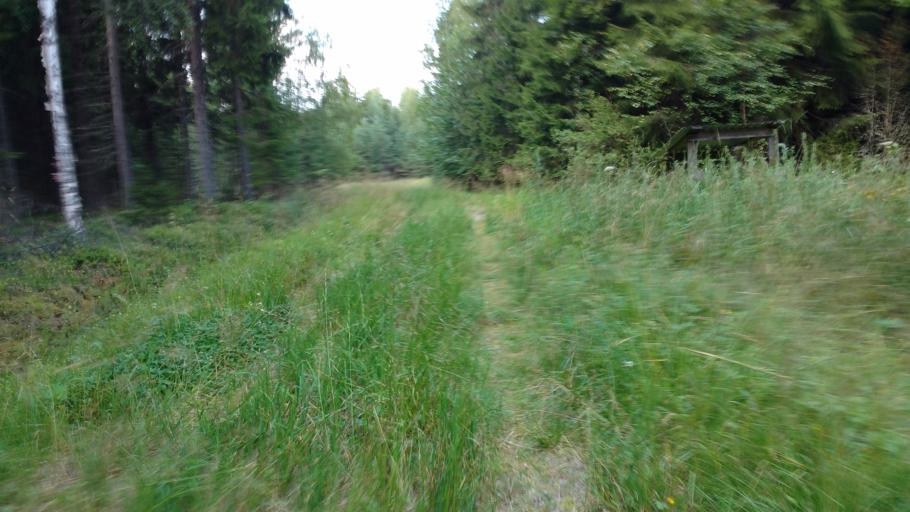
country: FI
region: Varsinais-Suomi
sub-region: Salo
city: Pertteli
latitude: 60.3930
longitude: 23.2283
